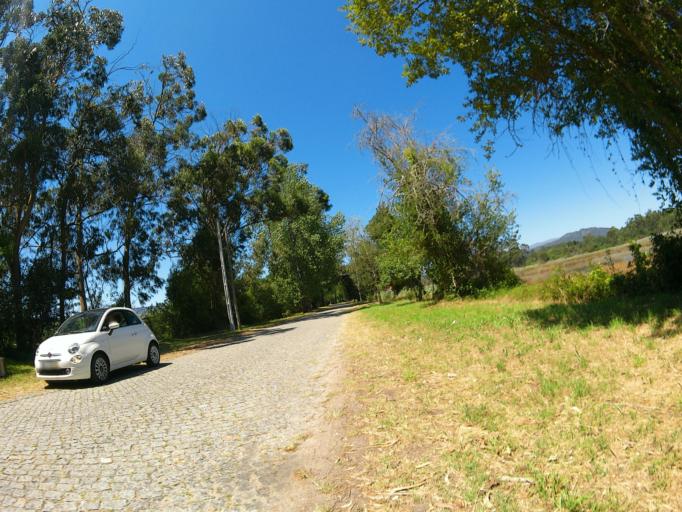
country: PT
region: Viana do Castelo
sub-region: Viana do Castelo
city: Darque
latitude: 41.6873
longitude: -8.7703
